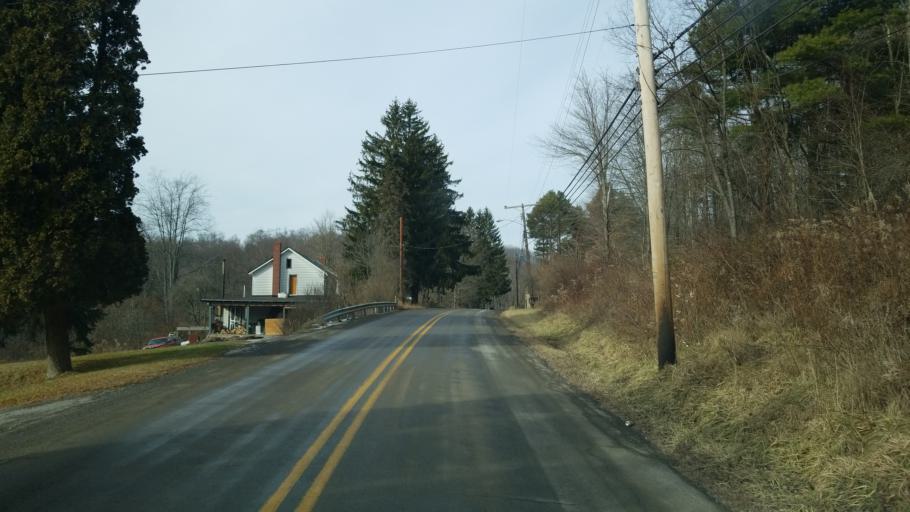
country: US
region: Pennsylvania
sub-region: Indiana County
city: Johnsonburg
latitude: 40.8252
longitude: -78.8330
